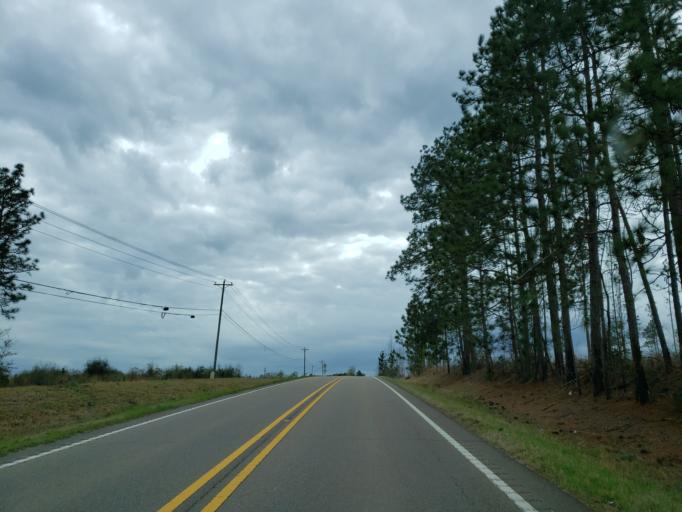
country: US
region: Mississippi
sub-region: Lamar County
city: Purvis
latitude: 31.2038
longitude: -89.3662
